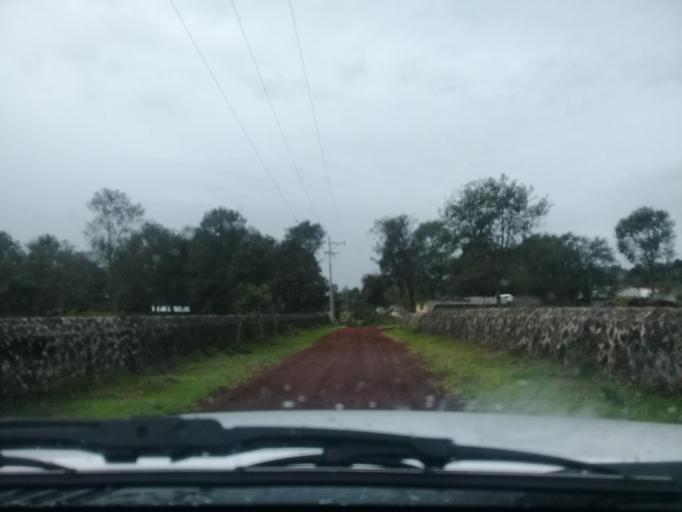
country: MX
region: Veracruz
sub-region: Acajete
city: La Joya
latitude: 19.6217
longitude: -97.0006
